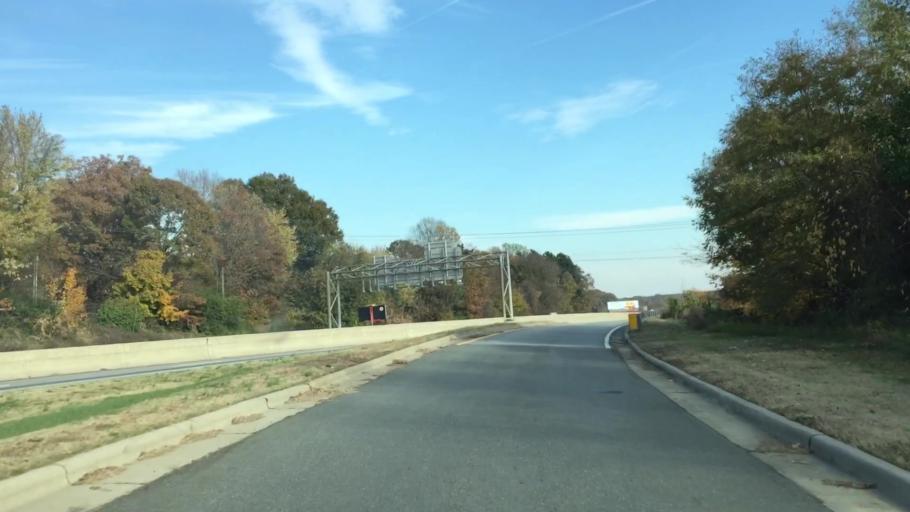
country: US
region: North Carolina
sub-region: Forsyth County
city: Winston-Salem
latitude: 36.0944
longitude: -80.2255
